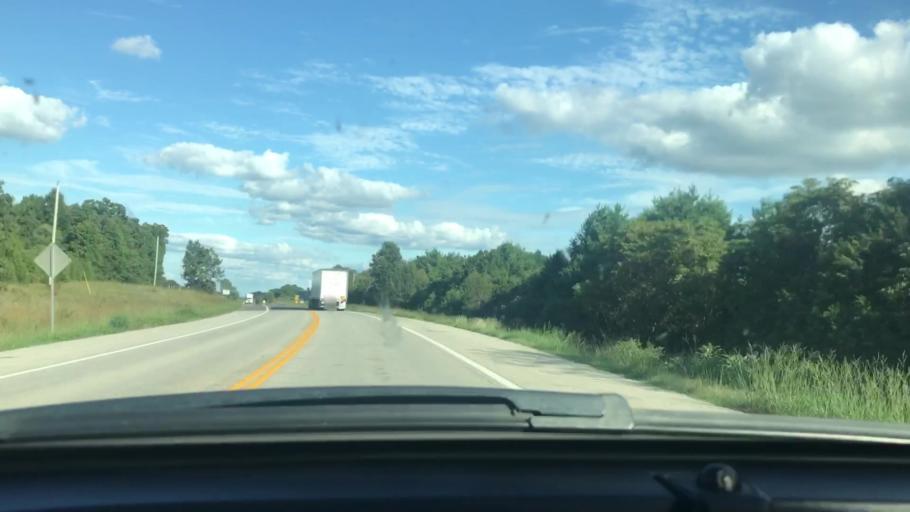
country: US
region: Missouri
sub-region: Oregon County
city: Thayer
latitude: 36.5891
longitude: -91.6394
